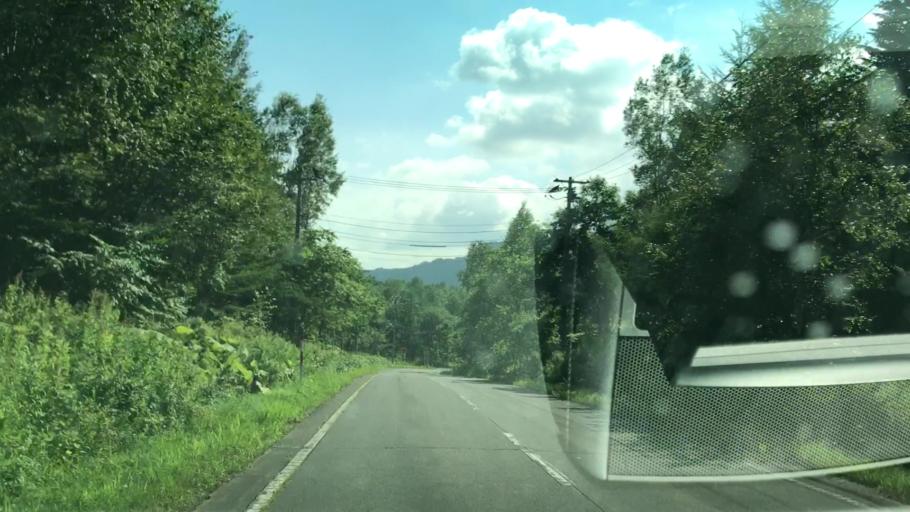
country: JP
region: Hokkaido
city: Shimo-furano
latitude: 42.8523
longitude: 142.4352
